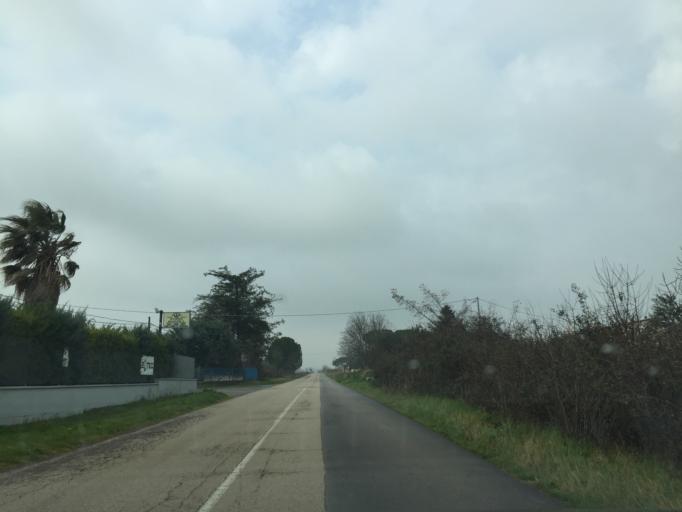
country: IT
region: Apulia
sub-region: Provincia di Foggia
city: Troia
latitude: 41.3816
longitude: 15.3754
